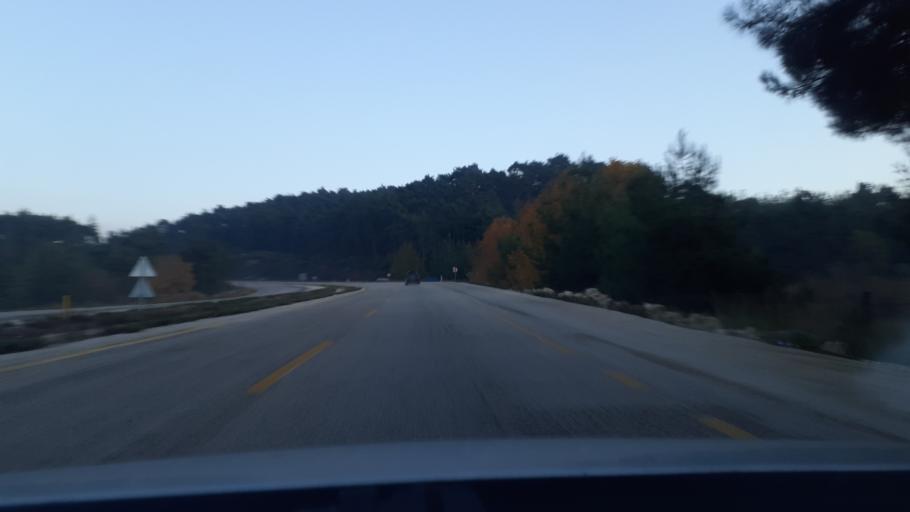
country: TR
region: Hatay
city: Yayladagi
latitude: 35.8921
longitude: 36.0858
